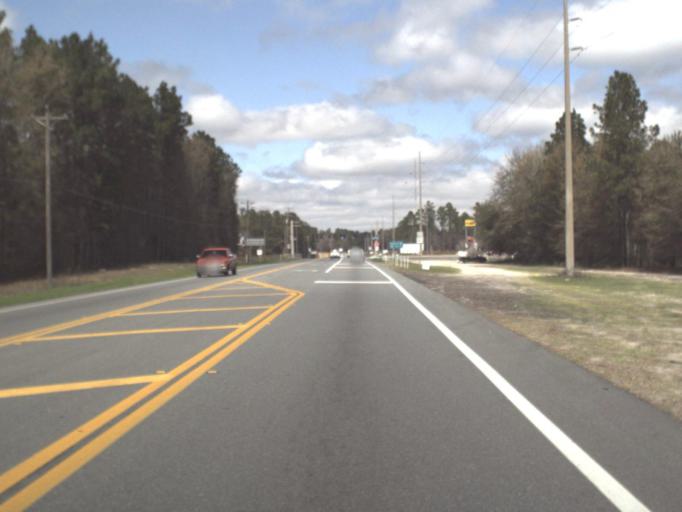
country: US
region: Florida
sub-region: Wakulla County
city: Crawfordville
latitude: 30.2609
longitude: -84.3622
